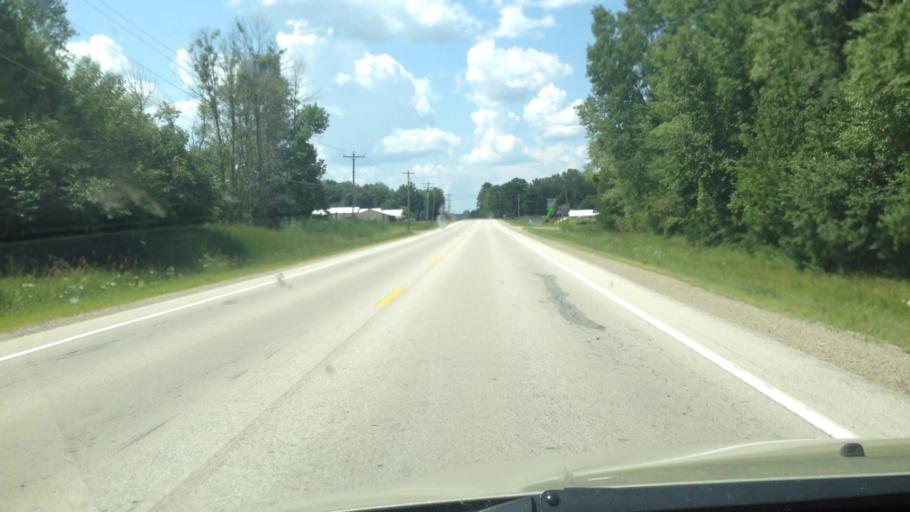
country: US
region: Wisconsin
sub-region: Brown County
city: Suamico
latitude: 44.6416
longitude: -88.0809
